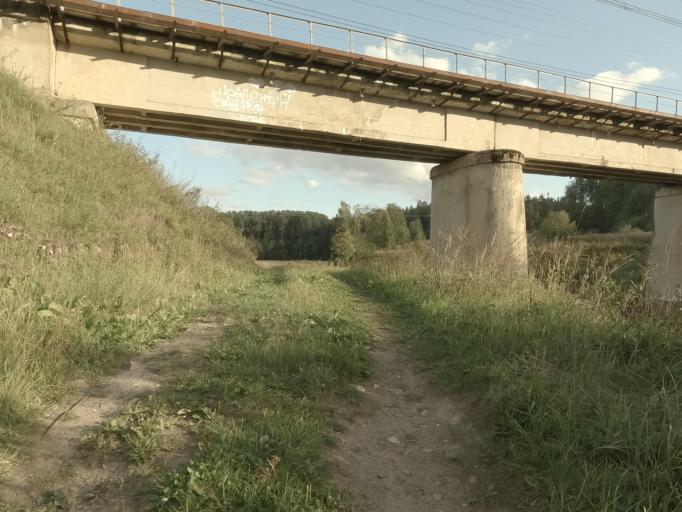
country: RU
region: Leningrad
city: Mga
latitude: 59.7520
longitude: 31.0280
